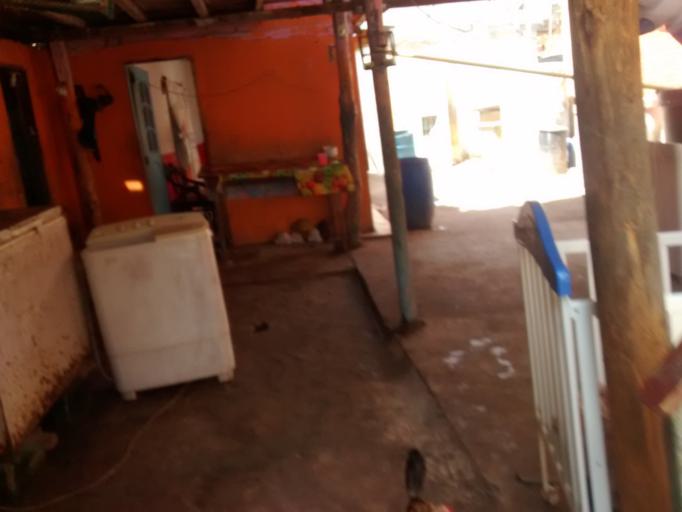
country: CO
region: Sucre
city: San Onofre
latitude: 9.7858
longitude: -75.8596
